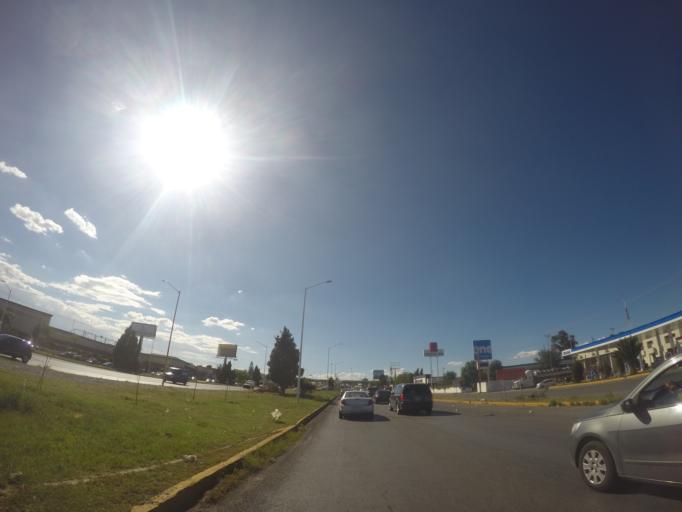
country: MX
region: San Luis Potosi
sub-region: San Luis Potosi
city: San Luis Potosi
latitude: 22.1481
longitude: -100.9522
